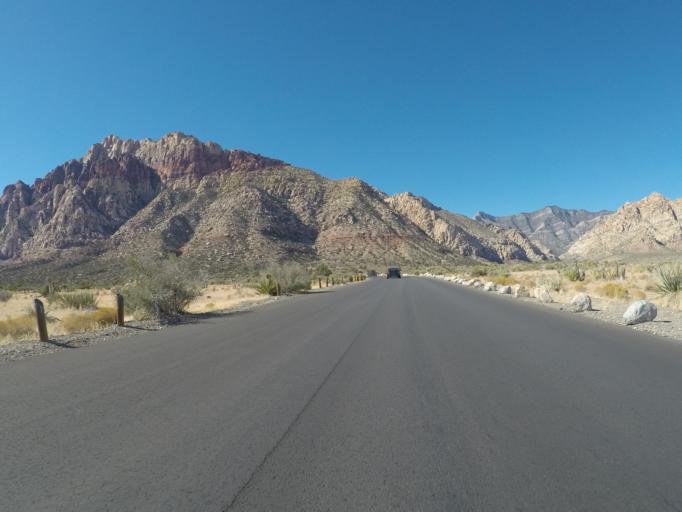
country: US
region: Nevada
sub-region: Clark County
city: Summerlin South
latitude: 36.1388
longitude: -115.4709
